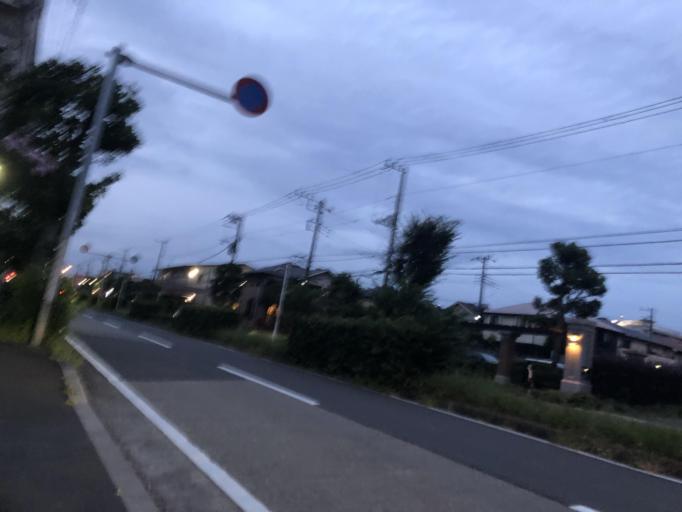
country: JP
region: Chiba
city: Funabashi
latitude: 35.7211
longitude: 139.9714
